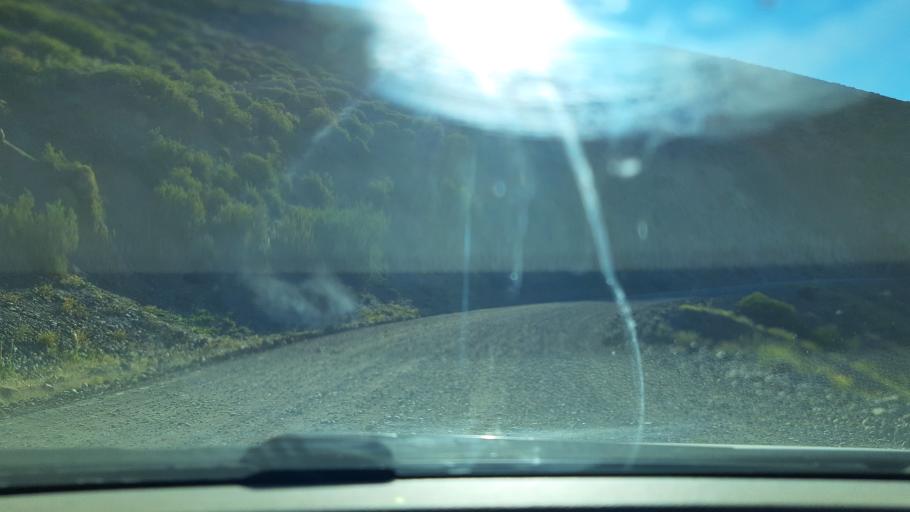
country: AR
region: Neuquen
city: Las Ovejas
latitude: -36.8081
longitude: -70.7213
